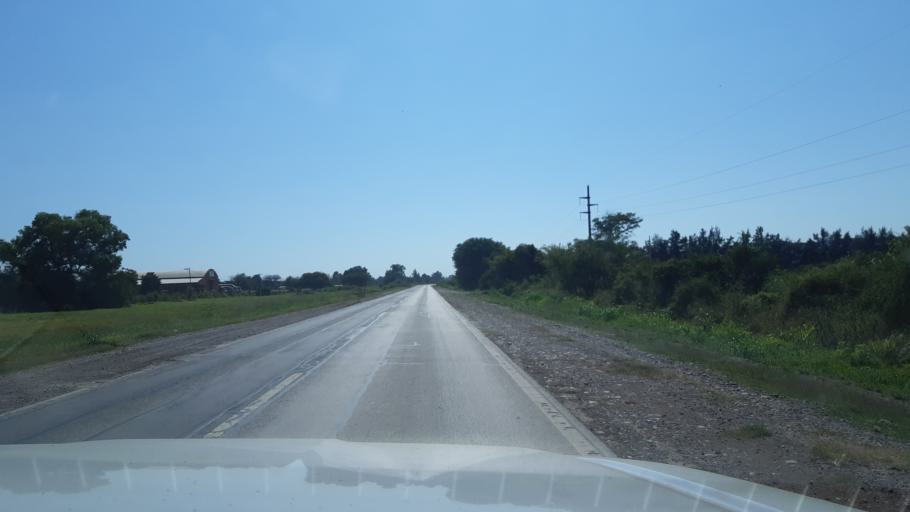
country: AR
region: Jujuy
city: La Mendieta
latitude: -24.4705
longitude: -65.0334
